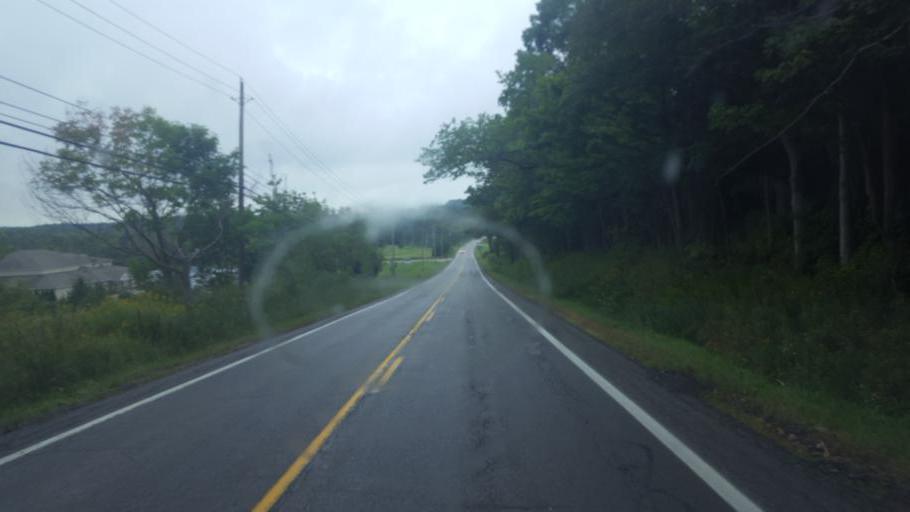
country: US
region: Ohio
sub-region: Geauga County
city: Burton
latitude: 41.5267
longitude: -81.1937
